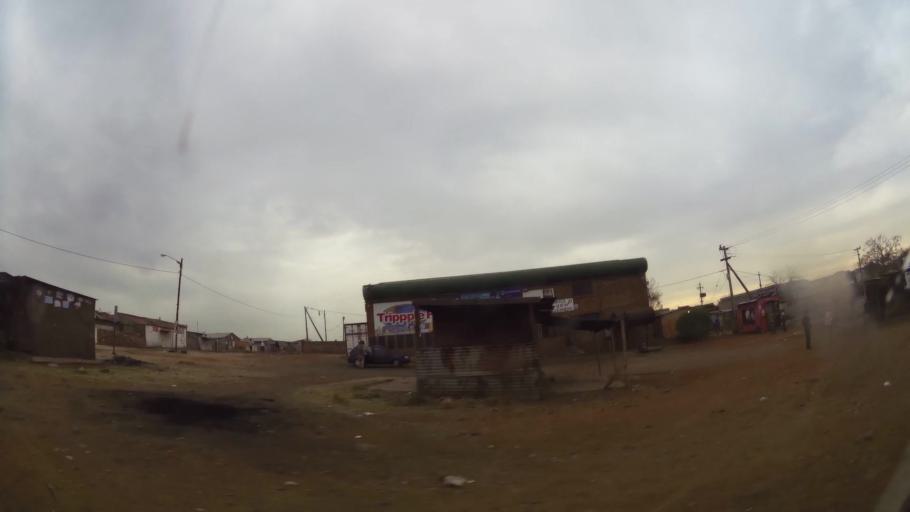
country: ZA
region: Gauteng
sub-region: Ekurhuleni Metropolitan Municipality
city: Germiston
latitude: -26.3800
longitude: 28.1766
